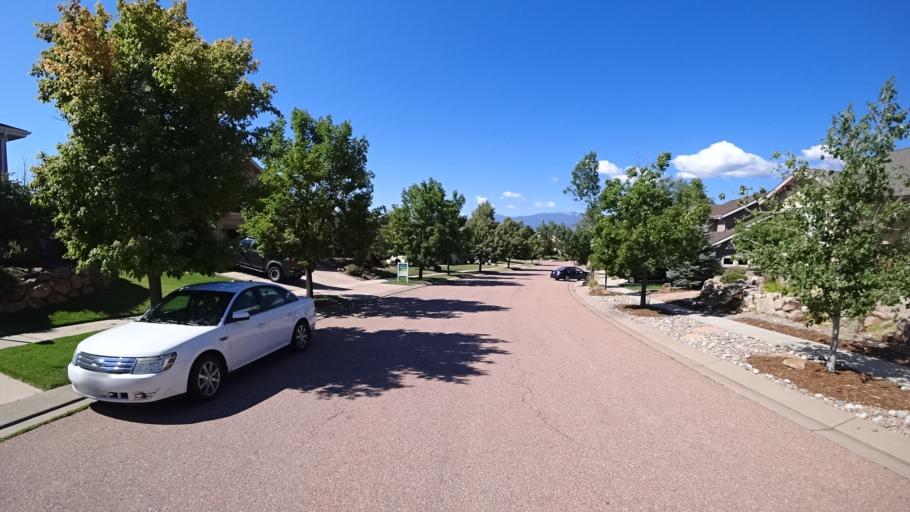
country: US
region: Colorado
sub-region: El Paso County
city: Gleneagle
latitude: 38.9721
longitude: -104.7808
